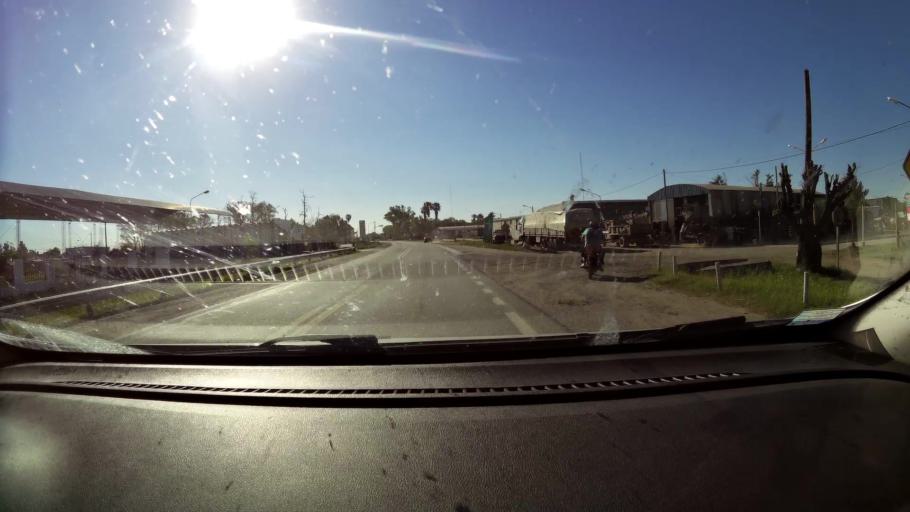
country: AR
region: Cordoba
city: San Francisco
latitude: -31.4206
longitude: -62.0606
